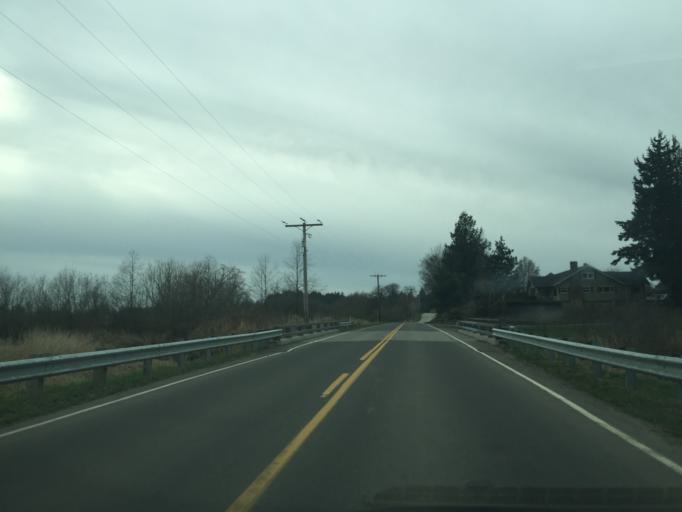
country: US
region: Washington
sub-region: Whatcom County
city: Nooksack
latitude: 48.9784
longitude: -122.3180
